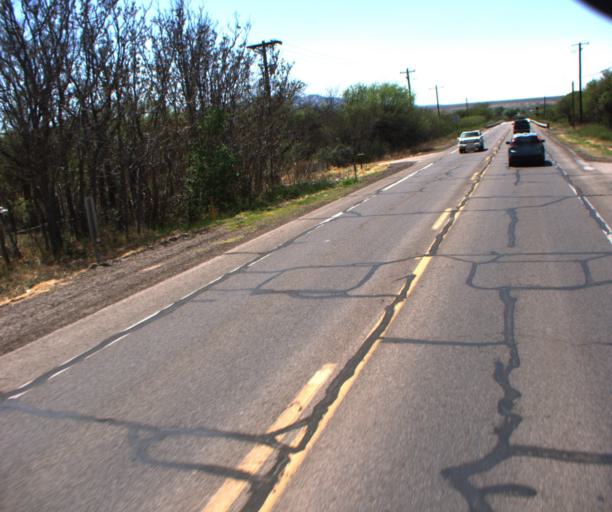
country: US
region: Arizona
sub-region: Cochise County
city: Saint David
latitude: 31.9054
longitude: -110.2431
